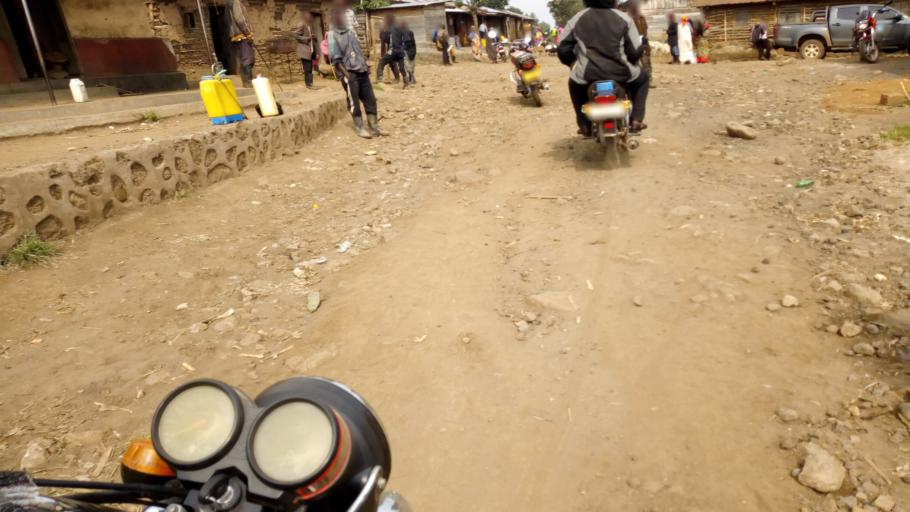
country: UG
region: Western Region
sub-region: Kisoro District
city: Kisoro
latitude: -1.3330
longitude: 29.6080
